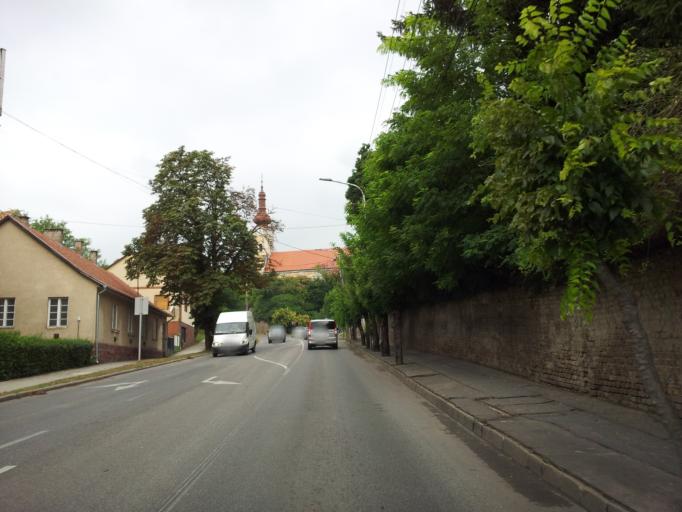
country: HU
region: Tolna
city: Tamasi
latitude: 46.6299
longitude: 18.2843
